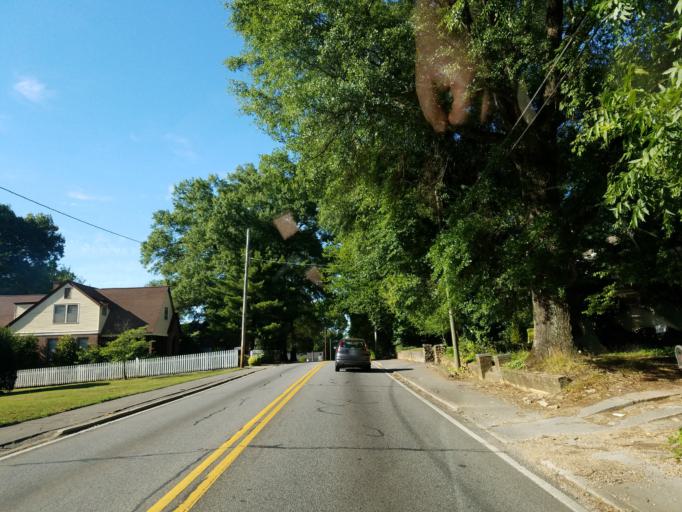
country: US
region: Georgia
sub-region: Gordon County
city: Calhoun
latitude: 34.5078
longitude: -84.9501
